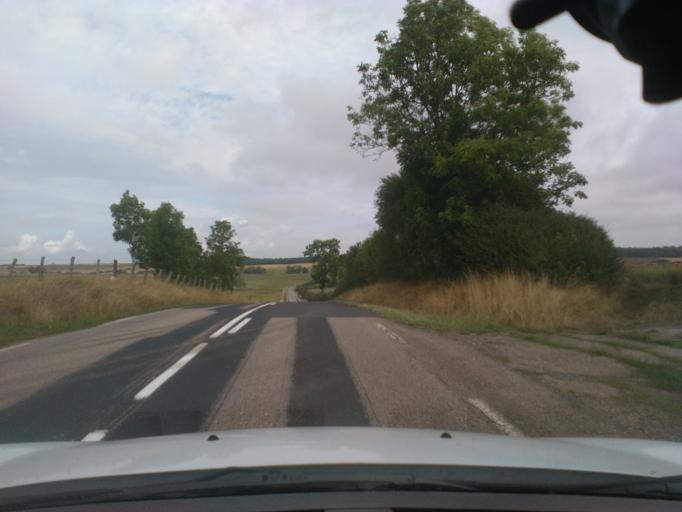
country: FR
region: Lorraine
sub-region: Departement de Meurthe-et-Moselle
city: Vezelise
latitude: 48.4257
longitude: 6.1264
